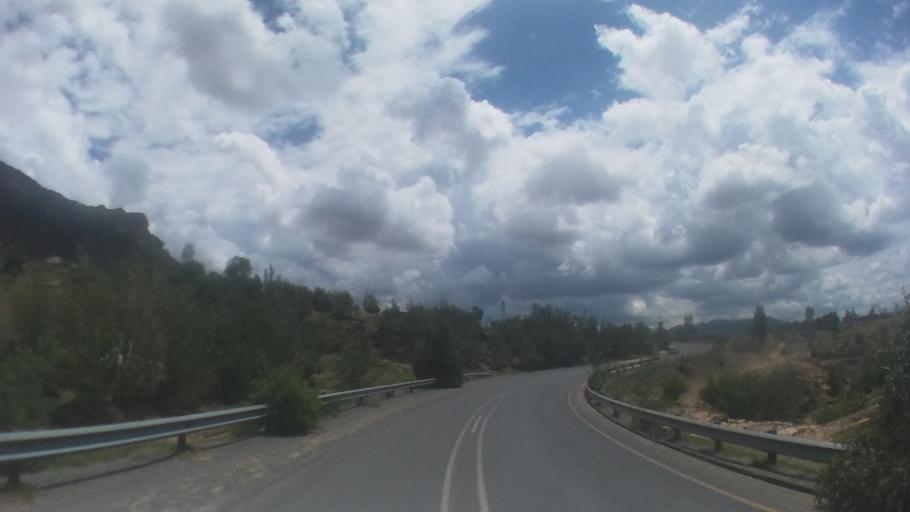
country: LS
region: Maseru
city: Maseru
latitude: -29.4163
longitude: 27.4730
